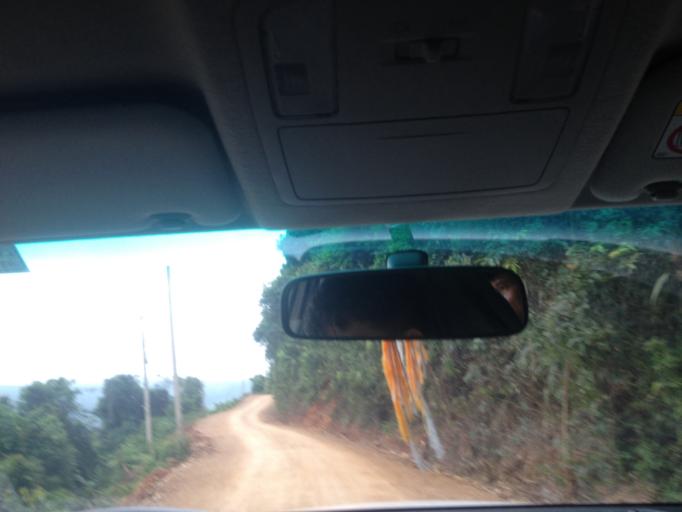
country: TH
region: Nan
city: Chaloem Phra Kiat
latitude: 19.9919
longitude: 101.1399
